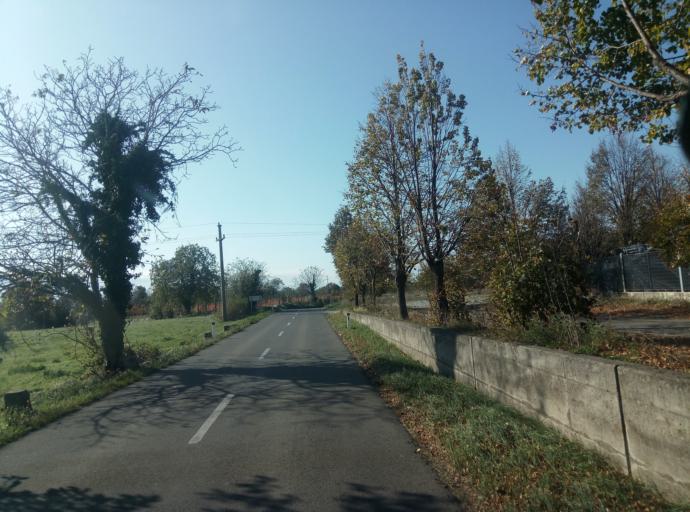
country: SI
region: Komen
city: Komen
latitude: 45.8145
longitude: 13.7416
